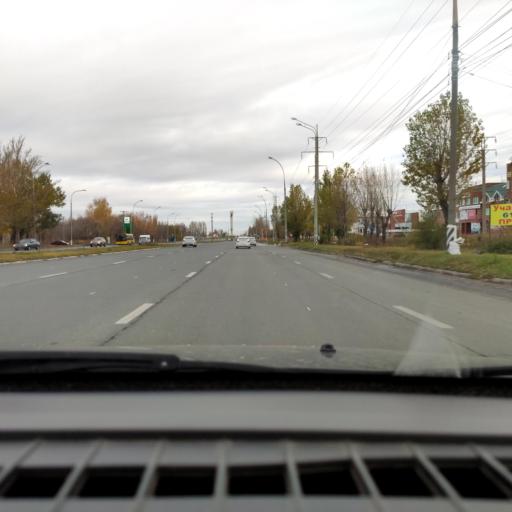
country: RU
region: Samara
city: Tol'yatti
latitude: 53.5481
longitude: 49.2865
